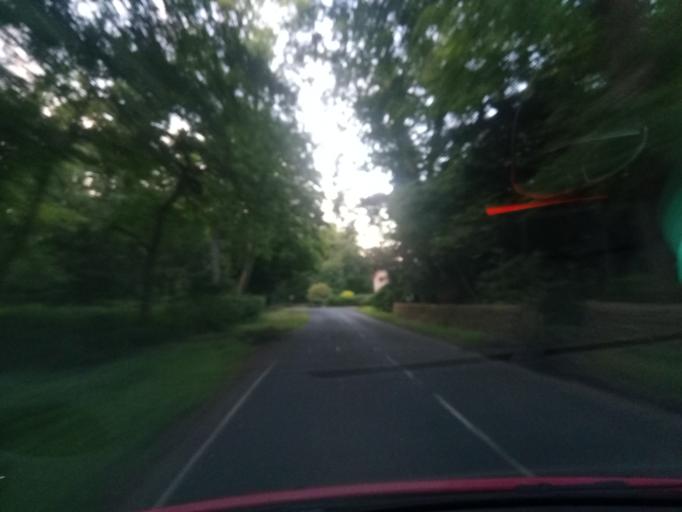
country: GB
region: England
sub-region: Northumberland
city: Bardon Mill
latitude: 54.9004
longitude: -2.3505
